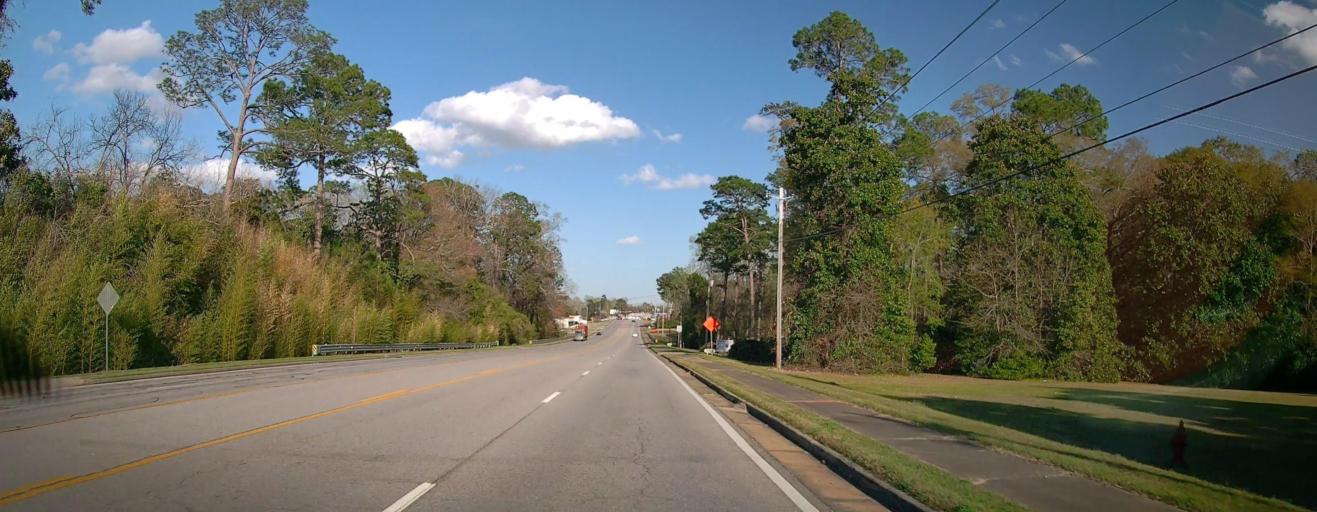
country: US
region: Georgia
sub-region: Toombs County
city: Vidalia
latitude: 32.2203
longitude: -82.4295
